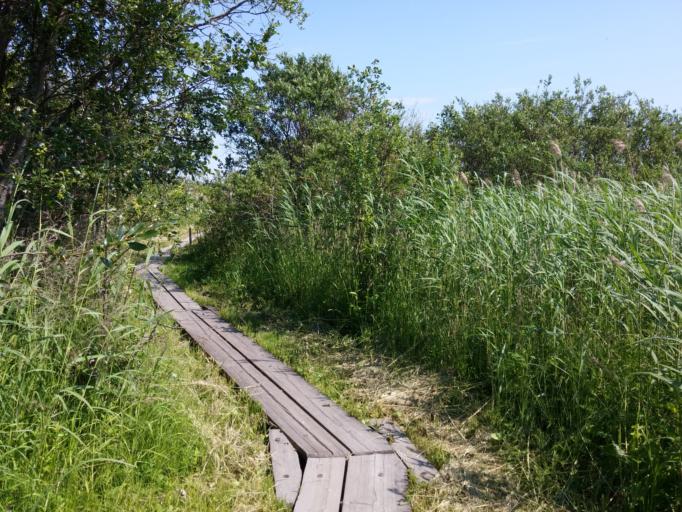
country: FI
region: Uusimaa
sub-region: Helsinki
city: Helsinki
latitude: 60.2130
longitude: 24.9917
